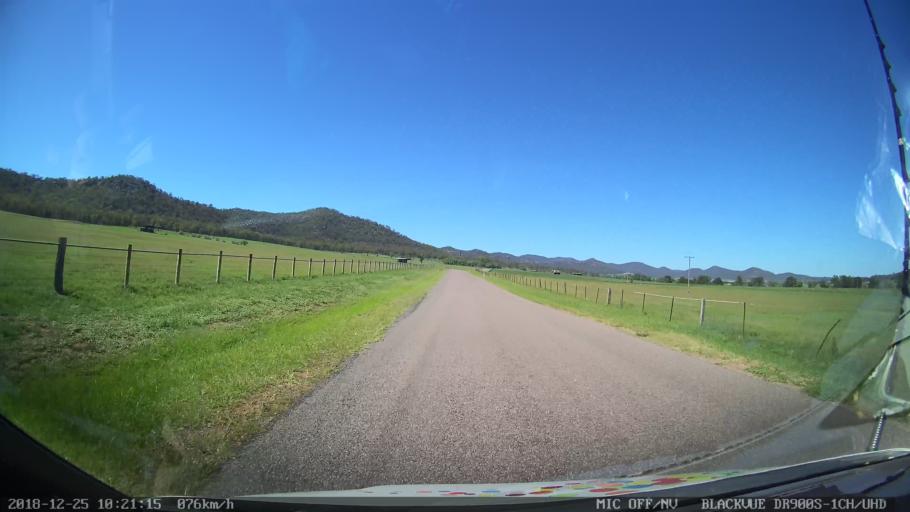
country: AU
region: New South Wales
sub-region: Muswellbrook
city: Denman
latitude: -32.3654
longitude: 150.5423
